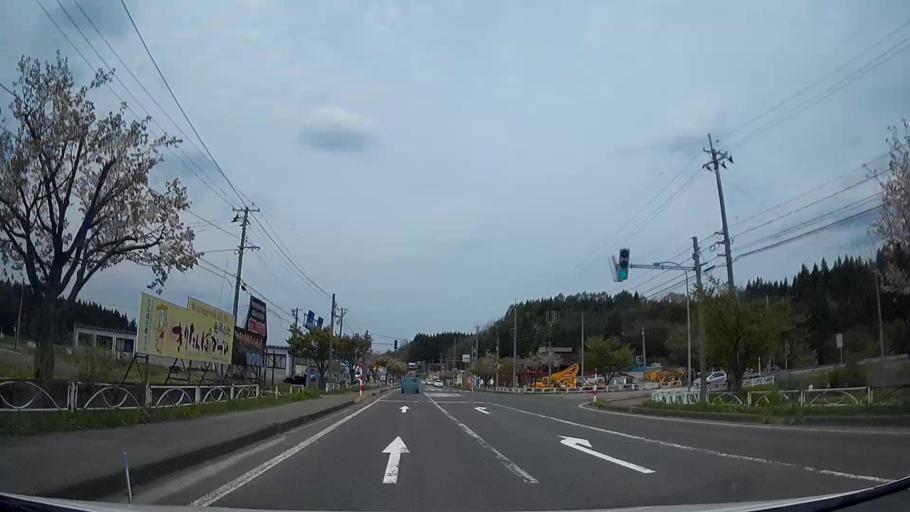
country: JP
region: Akita
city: Hanawa
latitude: 40.1665
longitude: 140.7906
